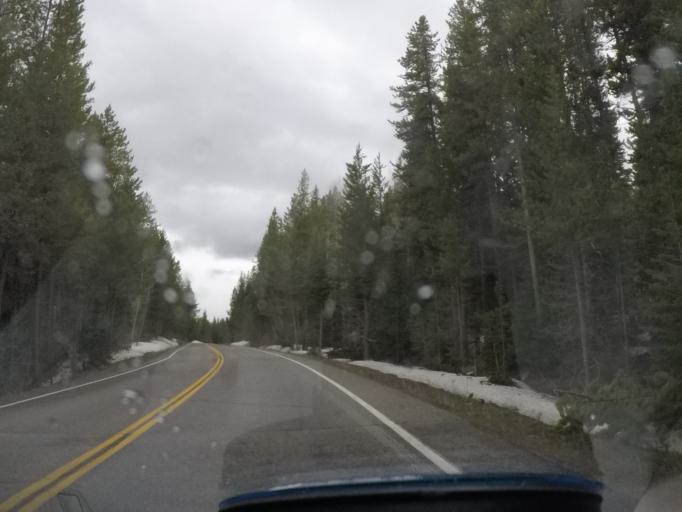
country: US
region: Wyoming
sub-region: Teton County
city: Moose Wilson Road
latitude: 43.9903
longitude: -110.6687
